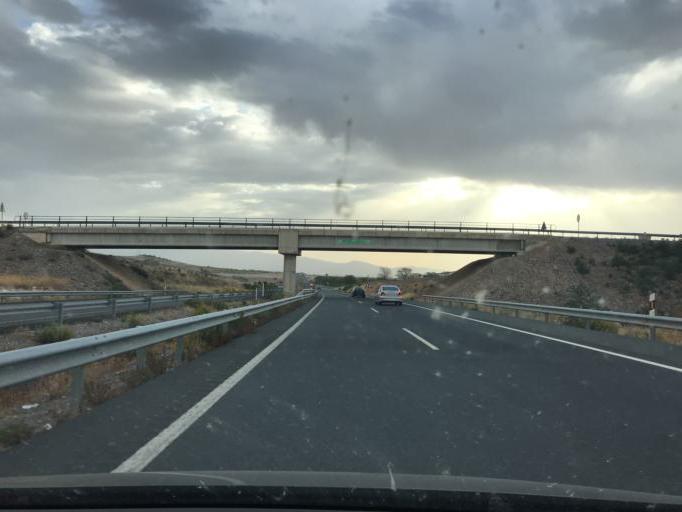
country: ES
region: Andalusia
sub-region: Provincia de Granada
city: Gor
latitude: 37.3908
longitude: -3.0427
